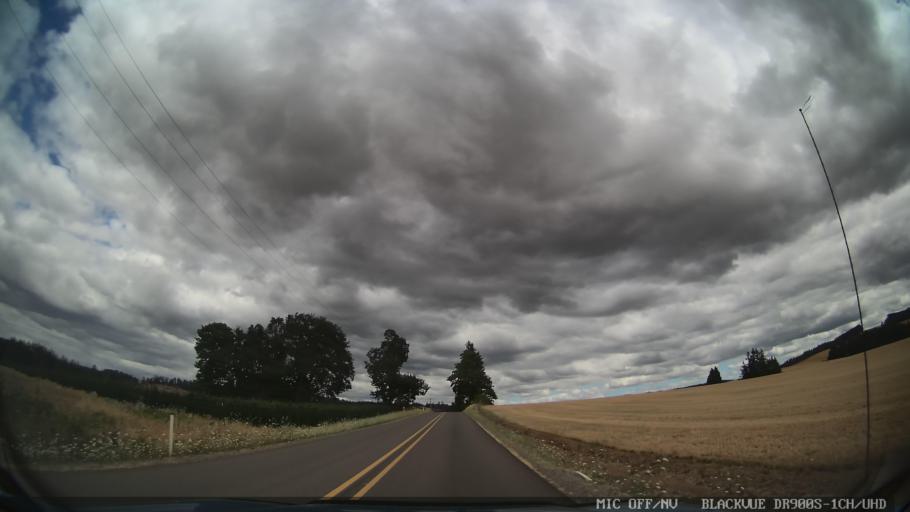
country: US
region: Oregon
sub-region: Marion County
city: Sublimity
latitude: 44.8724
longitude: -122.7256
